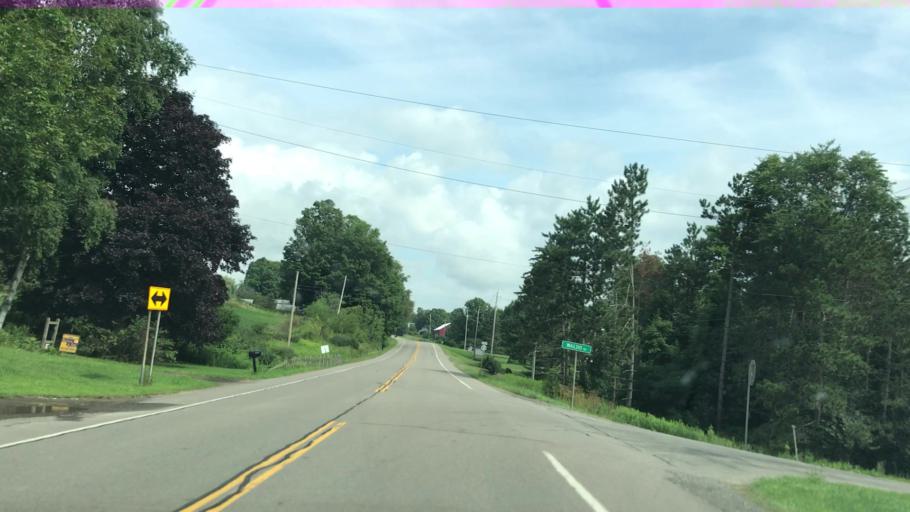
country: US
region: New York
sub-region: Ontario County
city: Naples
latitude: 42.5002
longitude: -77.2861
